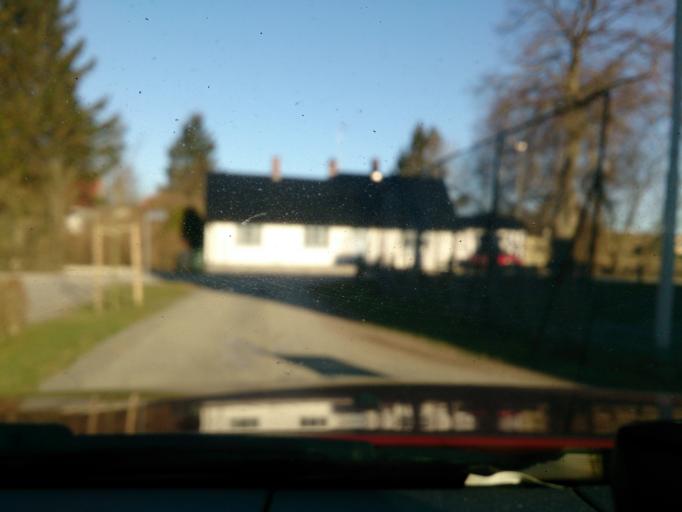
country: SE
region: Skane
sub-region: Skurups Kommun
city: Rydsgard
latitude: 55.4399
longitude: 13.6777
